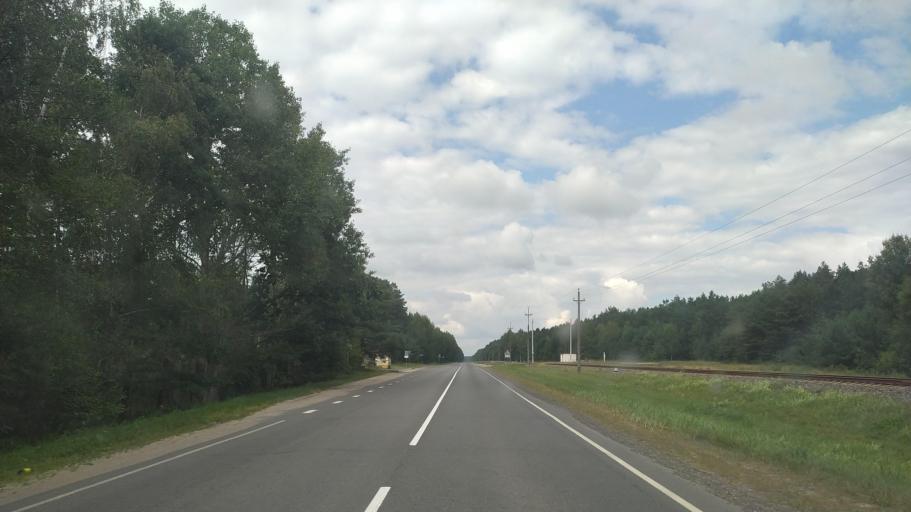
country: BY
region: Brest
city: Byelaazyorsk
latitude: 52.5407
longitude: 25.1378
